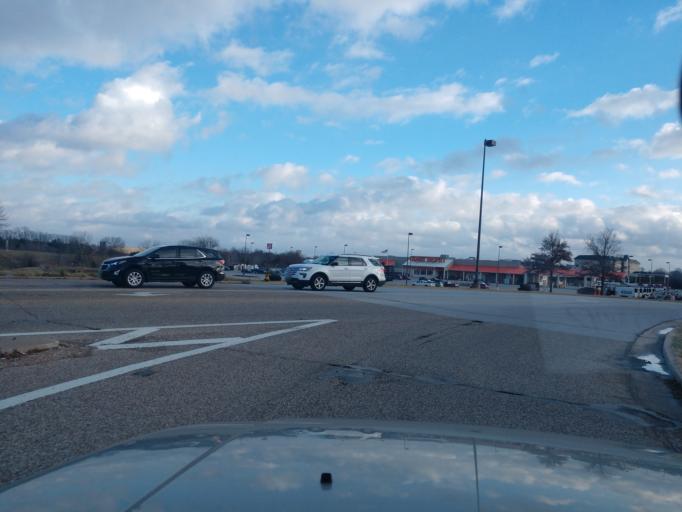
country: US
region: Illinois
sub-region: Adams County
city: Quincy
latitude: 39.9349
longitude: -91.3301
